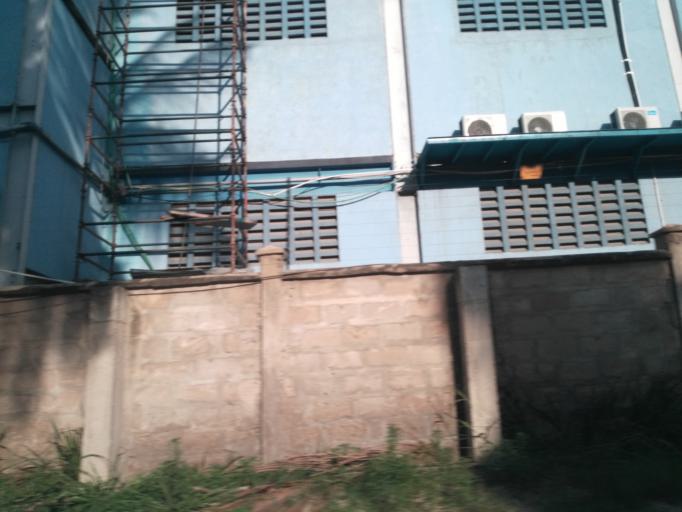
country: TZ
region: Dar es Salaam
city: Magomeni
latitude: -6.7563
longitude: 39.2353
